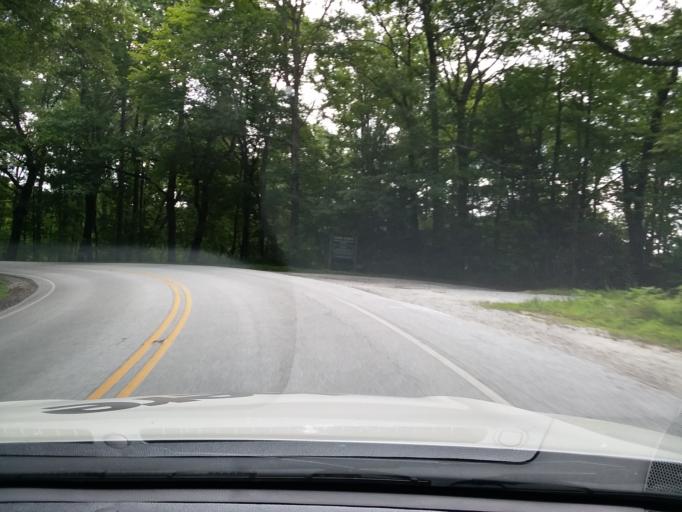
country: US
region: Georgia
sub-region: Rabun County
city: Mountain City
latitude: 35.0399
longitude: -83.2421
